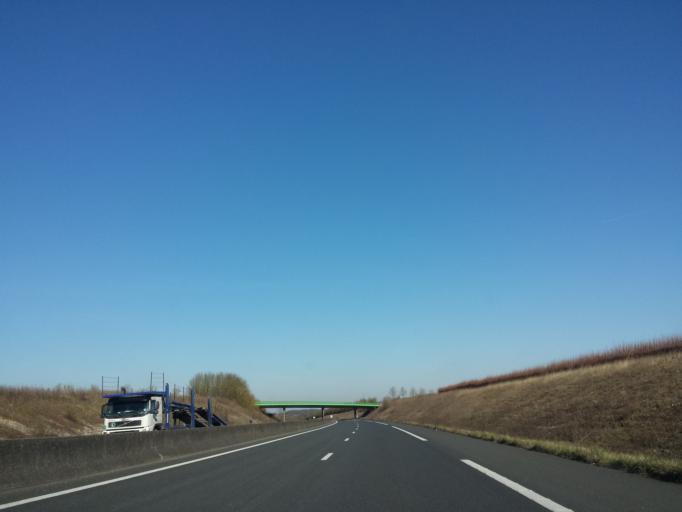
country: FR
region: Picardie
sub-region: Departement de l'Oise
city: Tille
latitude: 49.5203
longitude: 2.1865
